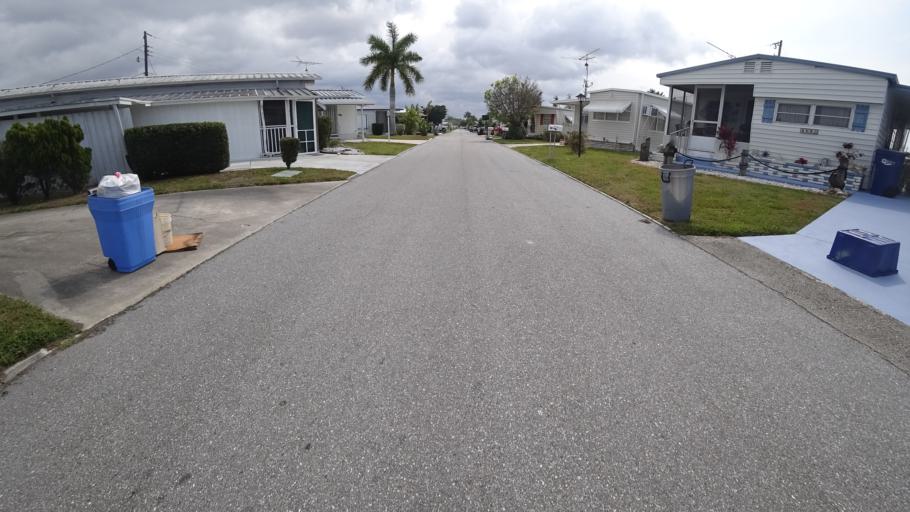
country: US
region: Florida
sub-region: Manatee County
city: South Bradenton
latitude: 27.4509
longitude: -82.5670
